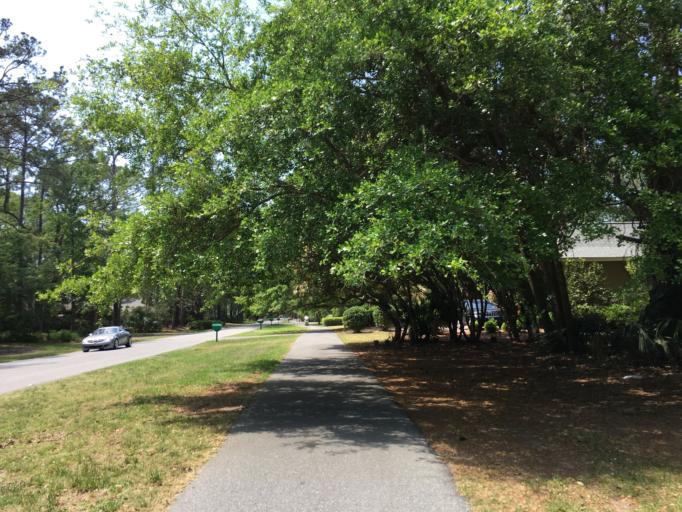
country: US
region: South Carolina
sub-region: Beaufort County
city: Hilton Head Island
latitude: 32.1229
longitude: -80.7972
